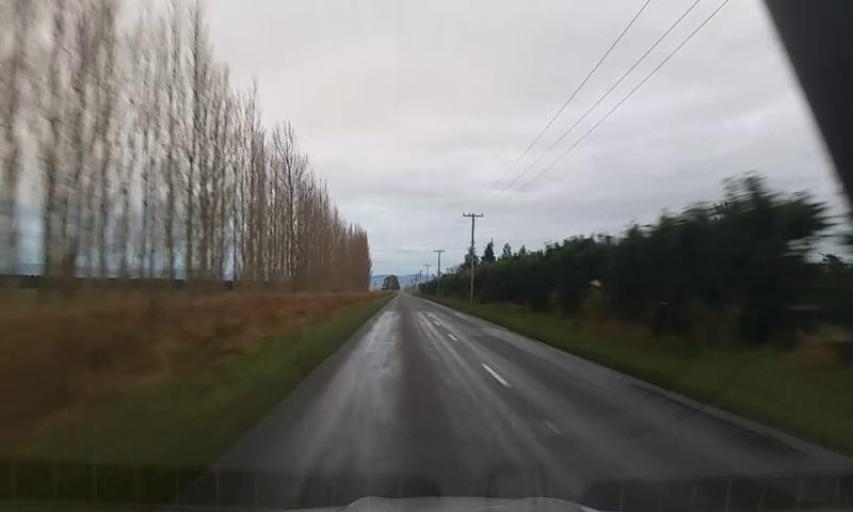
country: NZ
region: Canterbury
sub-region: Ashburton District
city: Methven
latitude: -43.7409
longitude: 171.7003
